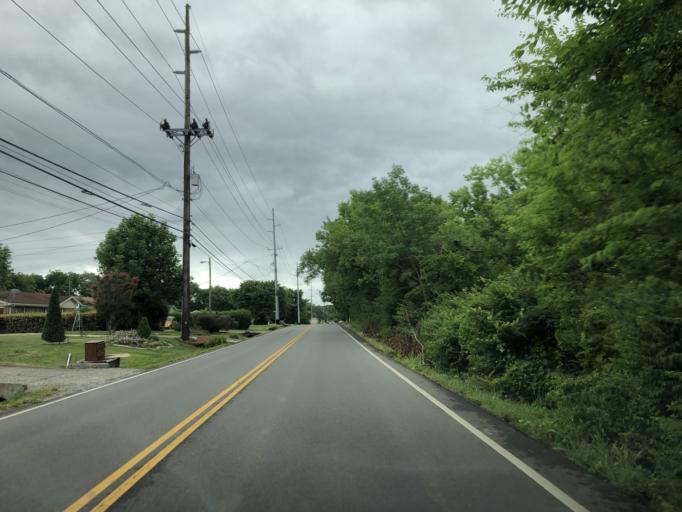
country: US
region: Tennessee
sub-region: Davidson County
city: Nashville
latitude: 36.2487
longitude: -86.7773
